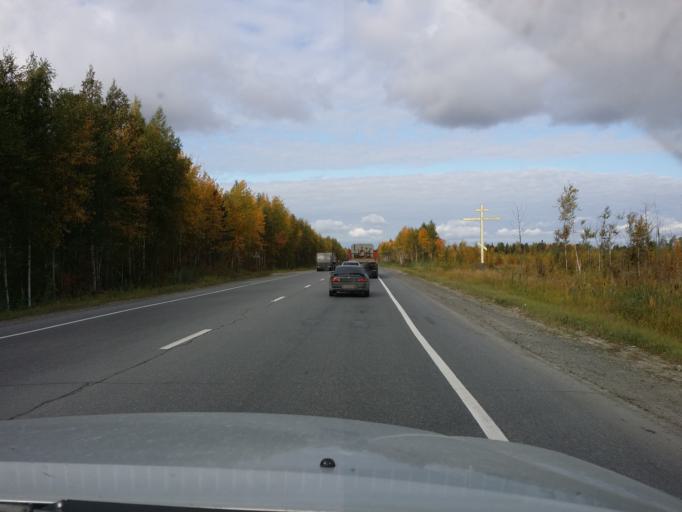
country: RU
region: Khanty-Mansiyskiy Avtonomnyy Okrug
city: Megion
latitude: 61.0623
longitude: 76.2763
